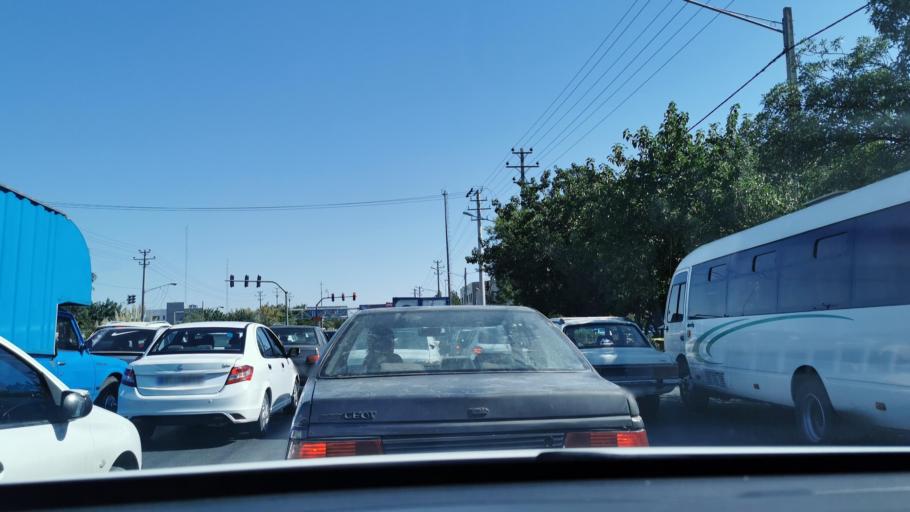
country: IR
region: Razavi Khorasan
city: Mashhad
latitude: 36.3343
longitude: 59.6256
